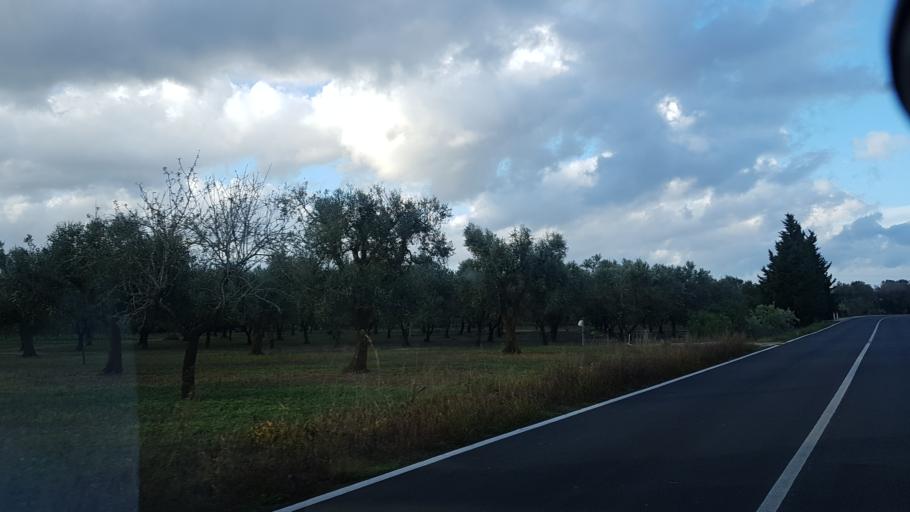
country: IT
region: Apulia
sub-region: Provincia di Brindisi
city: San Pietro Vernotico
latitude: 40.5140
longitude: 18.0112
